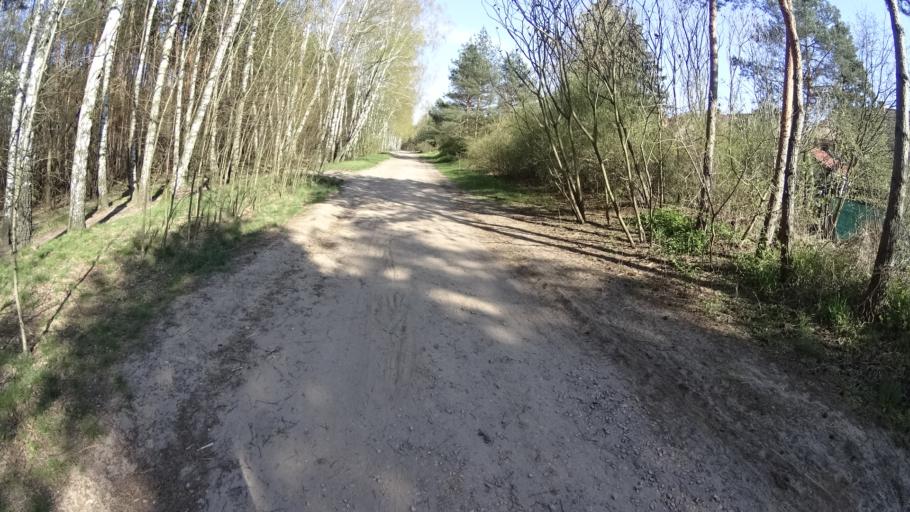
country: PL
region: Masovian Voivodeship
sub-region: Powiat warszawski zachodni
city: Babice
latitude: 52.2542
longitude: 20.8639
